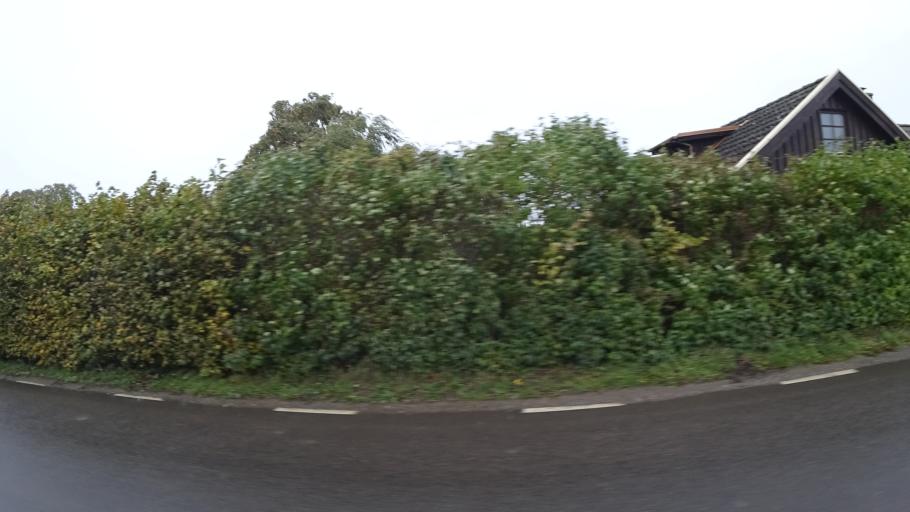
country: SE
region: Skane
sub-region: Kavlinge Kommun
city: Kaevlinge
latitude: 55.8206
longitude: 13.1154
